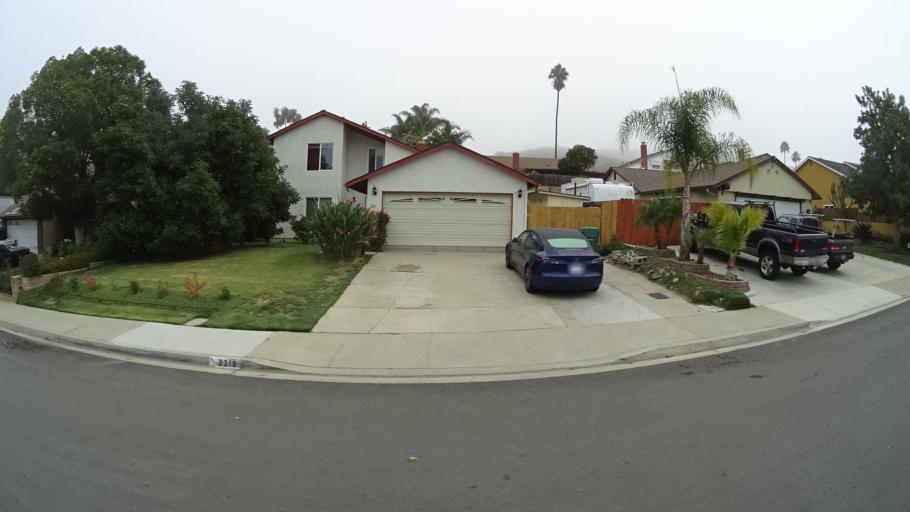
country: US
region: California
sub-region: San Diego County
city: Rancho San Diego
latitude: 32.7268
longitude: -116.9585
